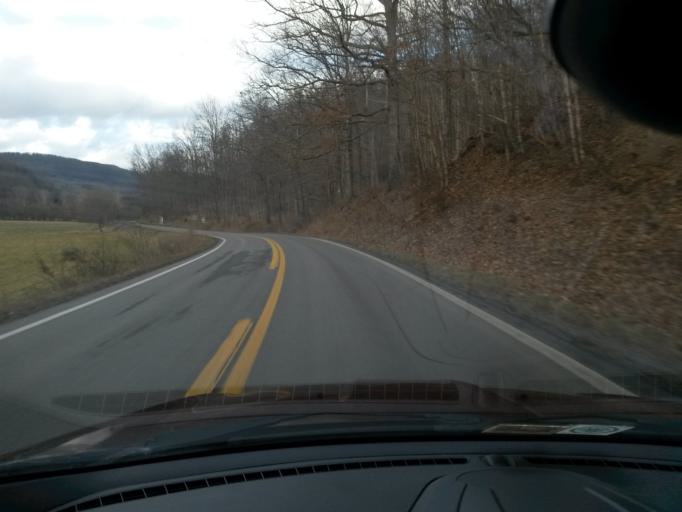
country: US
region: West Virginia
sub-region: Monroe County
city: Union
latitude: 37.5521
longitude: -80.5726
